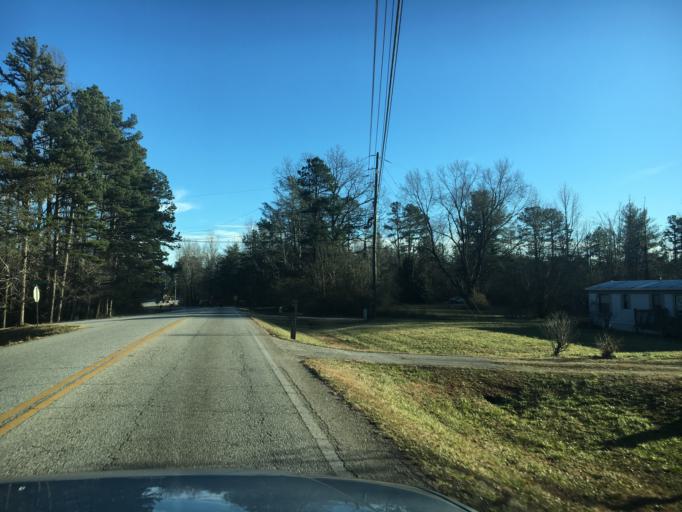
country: US
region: Georgia
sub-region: Habersham County
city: Demorest
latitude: 34.5544
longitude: -83.5731
